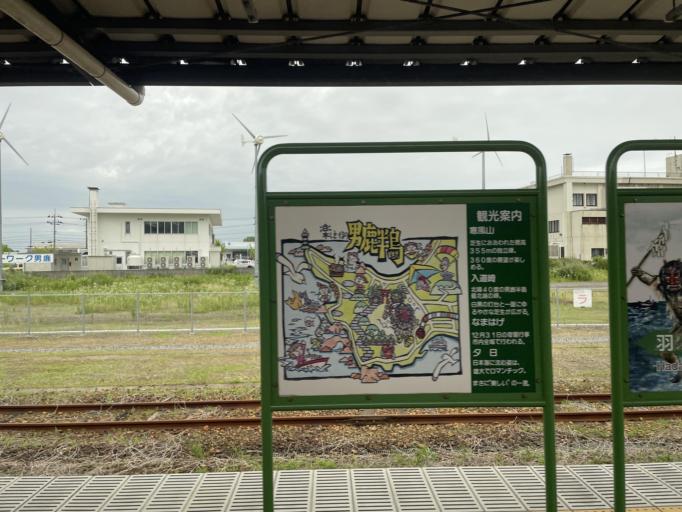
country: JP
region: Akita
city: Tenno
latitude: 39.8844
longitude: 139.8485
